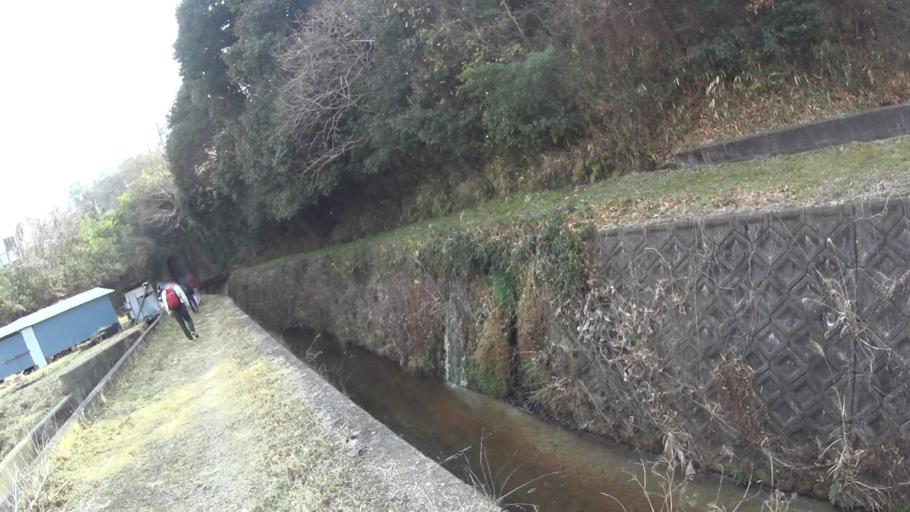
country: JP
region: Nara
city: Nara-shi
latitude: 34.7102
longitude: 135.8284
